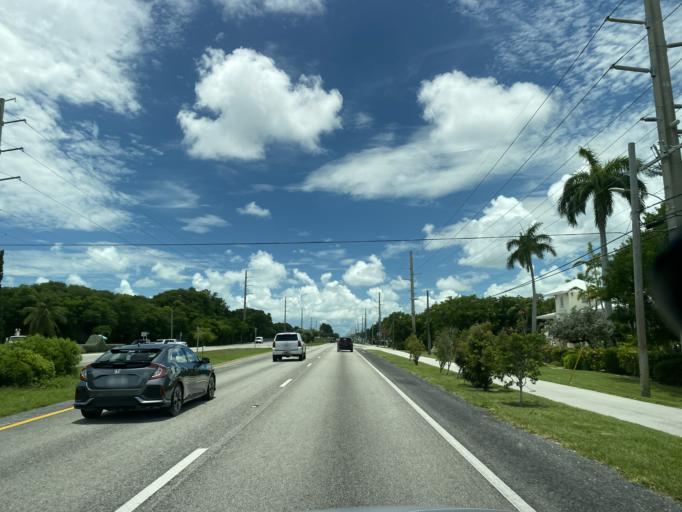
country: US
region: Florida
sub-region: Monroe County
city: Key Largo
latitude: 25.1409
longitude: -80.3998
